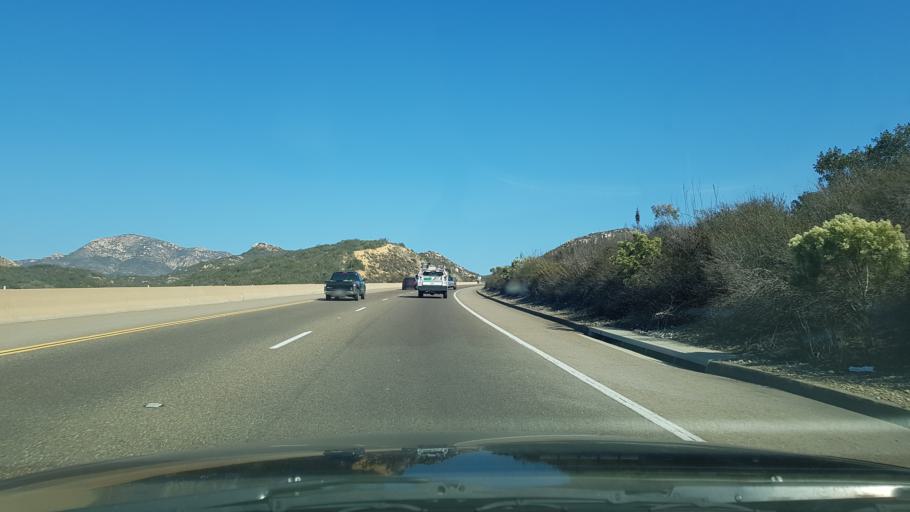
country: US
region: California
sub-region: San Diego County
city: Poway
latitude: 32.9507
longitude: -116.9852
